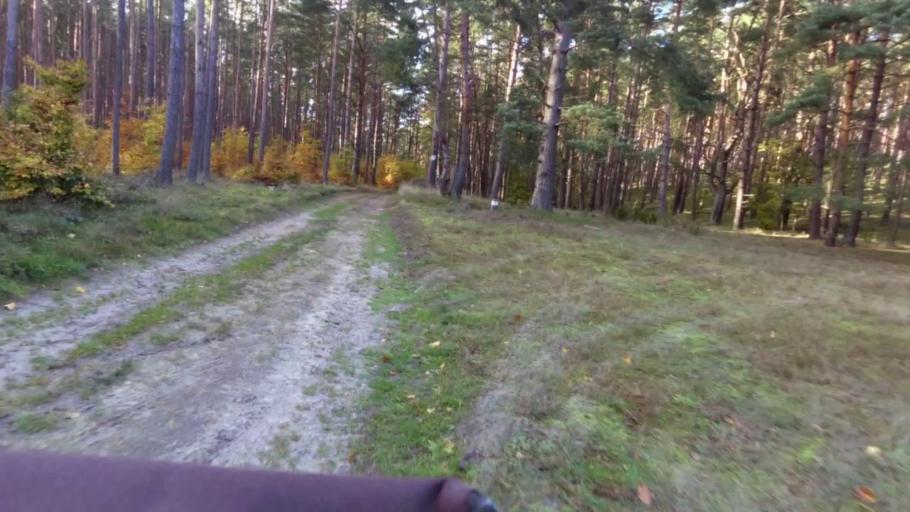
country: PL
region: West Pomeranian Voivodeship
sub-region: Powiat kamienski
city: Miedzyzdroje
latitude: 53.8702
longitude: 14.5240
